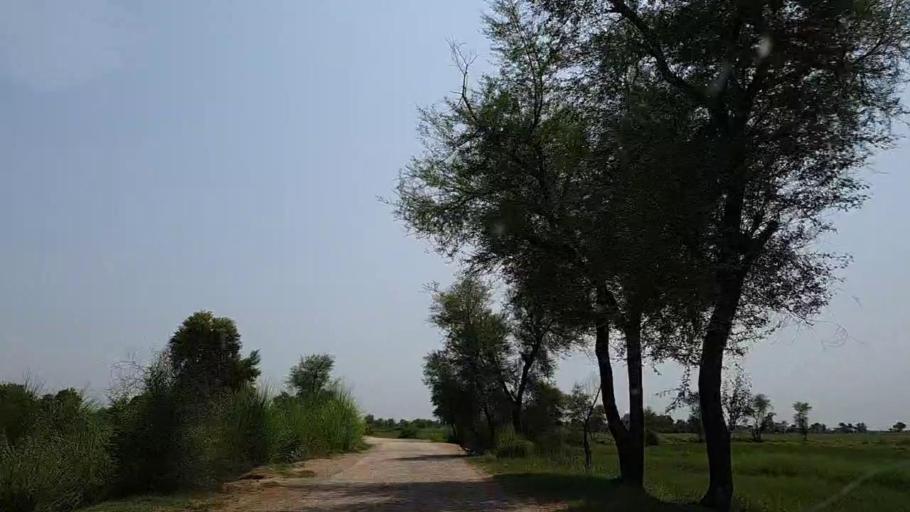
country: PK
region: Sindh
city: Adilpur
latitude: 27.9216
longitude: 69.3744
